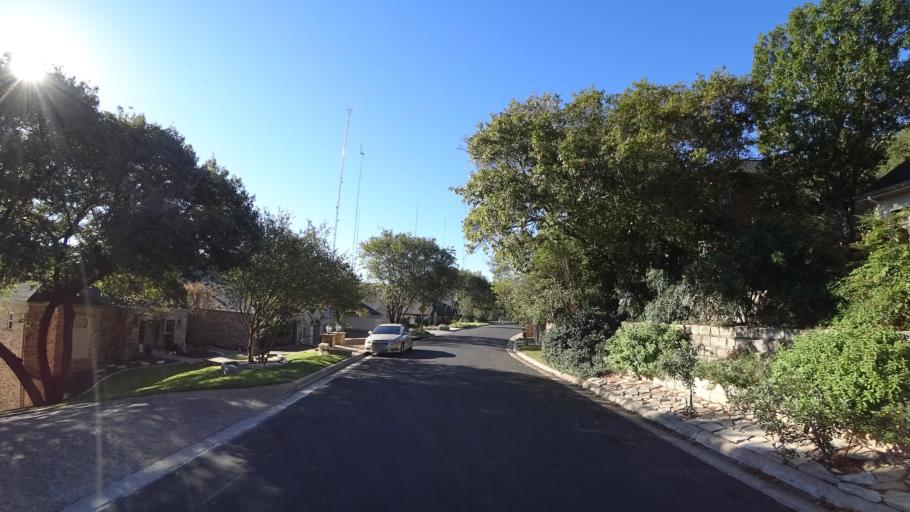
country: US
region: Texas
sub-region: Travis County
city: West Lake Hills
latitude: 30.3307
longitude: -97.8025
